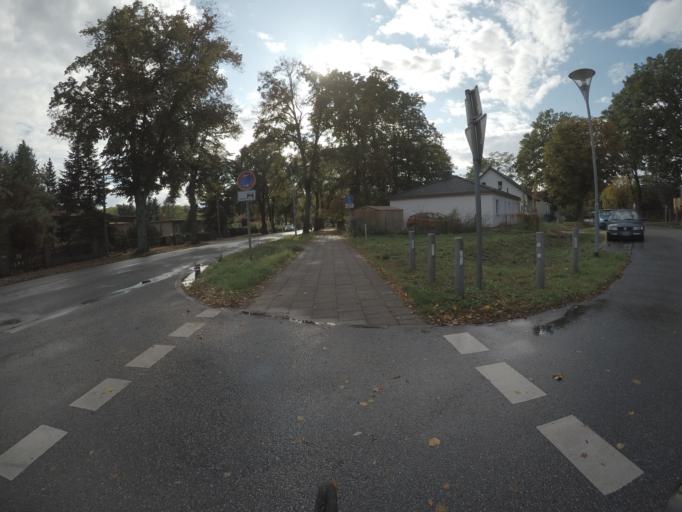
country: DE
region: Brandenburg
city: Strausberg
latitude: 52.5444
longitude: 13.8578
